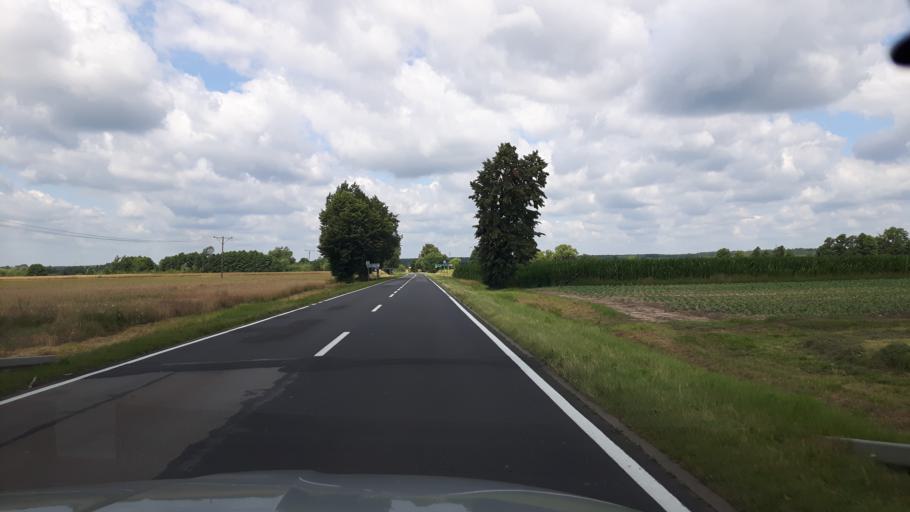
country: PL
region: Masovian Voivodeship
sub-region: Powiat ostrowski
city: Brok
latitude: 52.7011
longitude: 21.9115
